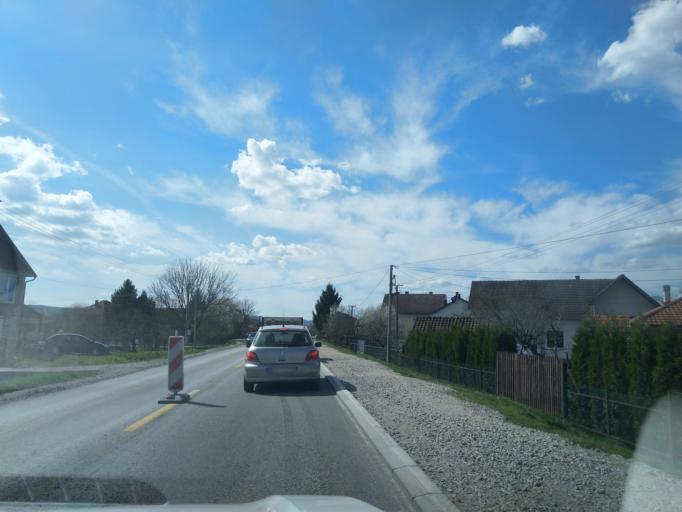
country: RS
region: Central Serbia
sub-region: Zlatiborski Okrug
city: Pozega
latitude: 43.8306
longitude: 20.0572
